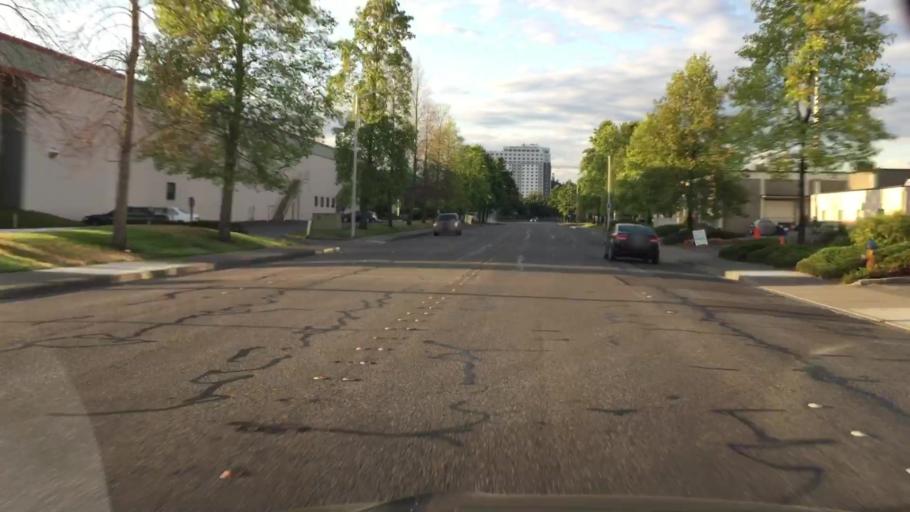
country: US
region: Washington
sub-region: King County
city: Tukwila
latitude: 47.4499
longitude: -122.2507
